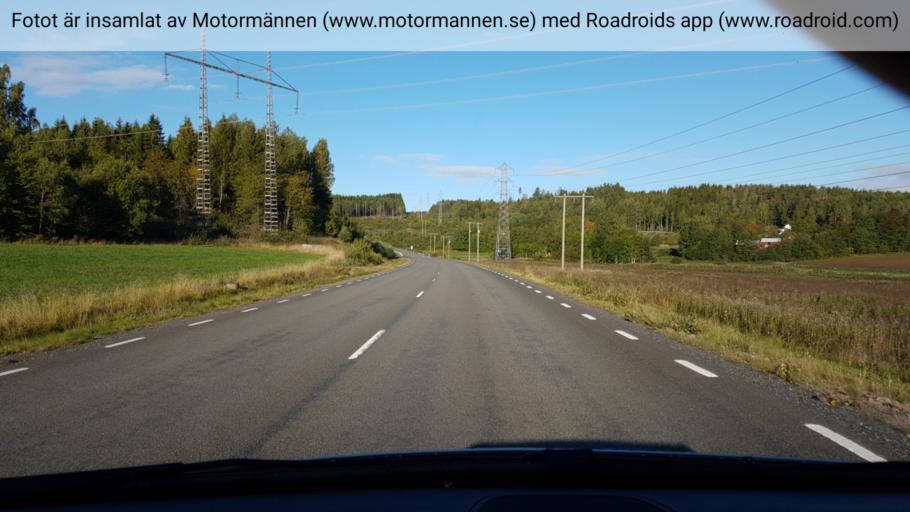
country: SE
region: Vaestra Goetaland
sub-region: Skovde Kommun
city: Stopen
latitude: 58.5368
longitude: 13.7515
